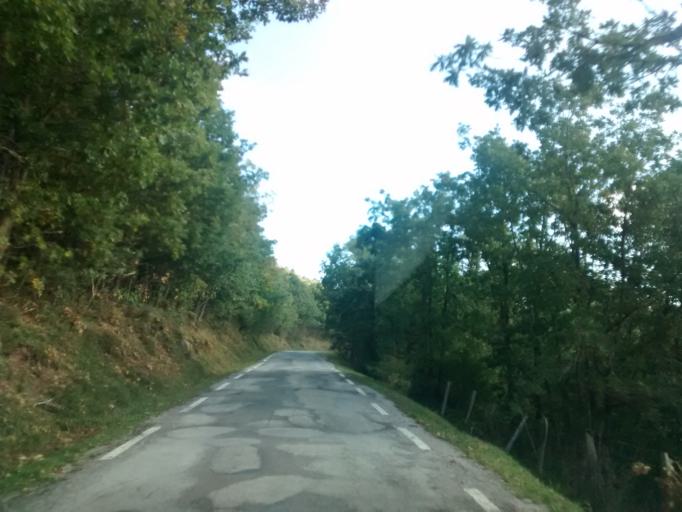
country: ES
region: Castille and Leon
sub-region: Provincia de Burgos
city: Arija
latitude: 42.9266
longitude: -4.0256
